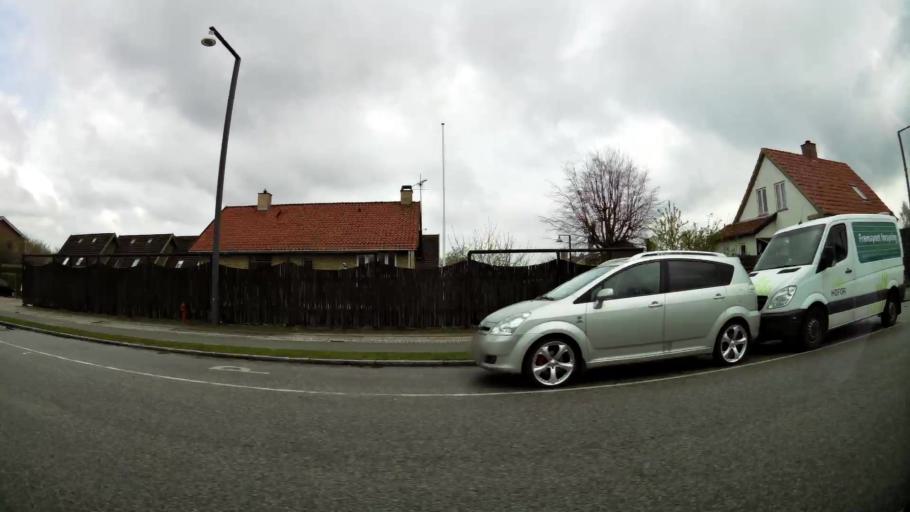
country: DK
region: Capital Region
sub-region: Rodovre Kommune
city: Rodovre
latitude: 55.6775
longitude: 12.4639
